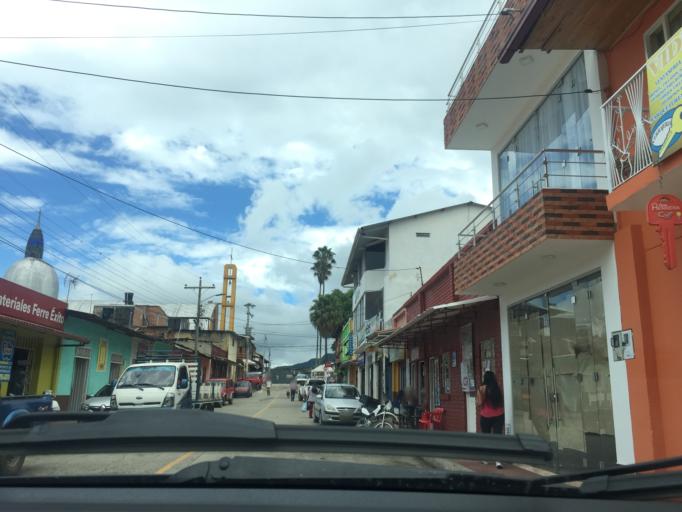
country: CO
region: Cundinamarca
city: Supata
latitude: 5.0612
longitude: -74.2362
